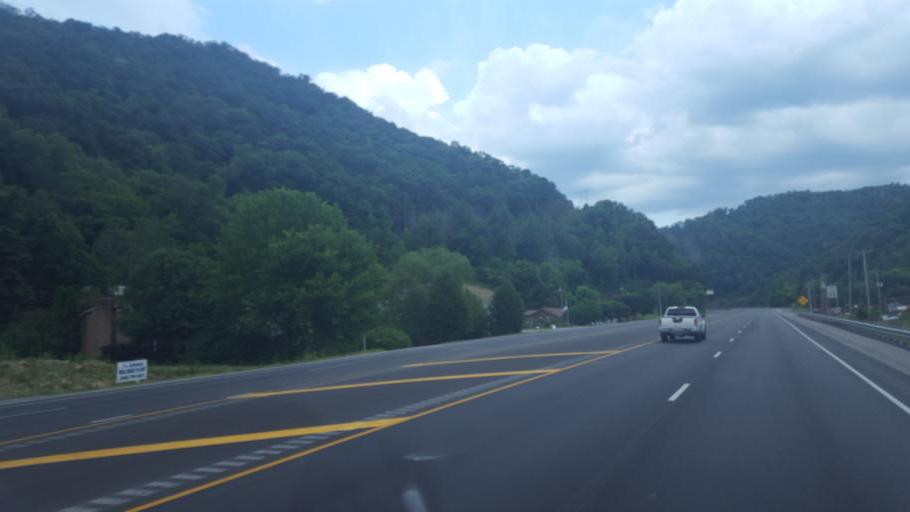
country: US
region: Kentucky
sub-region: Pike County
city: Pikeville
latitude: 37.3594
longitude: -82.5551
